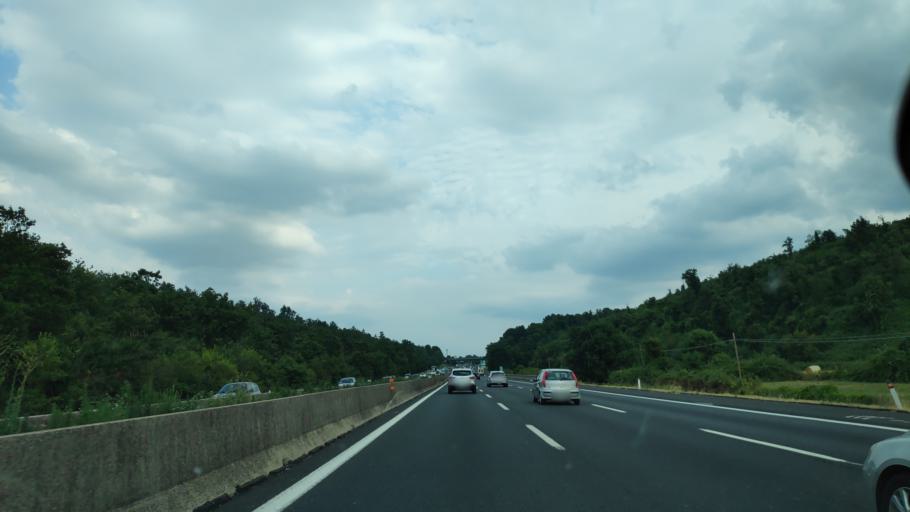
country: IT
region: Latium
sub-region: Provincia di Frosinone
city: Sgurgola
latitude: 41.6917
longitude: 13.1779
